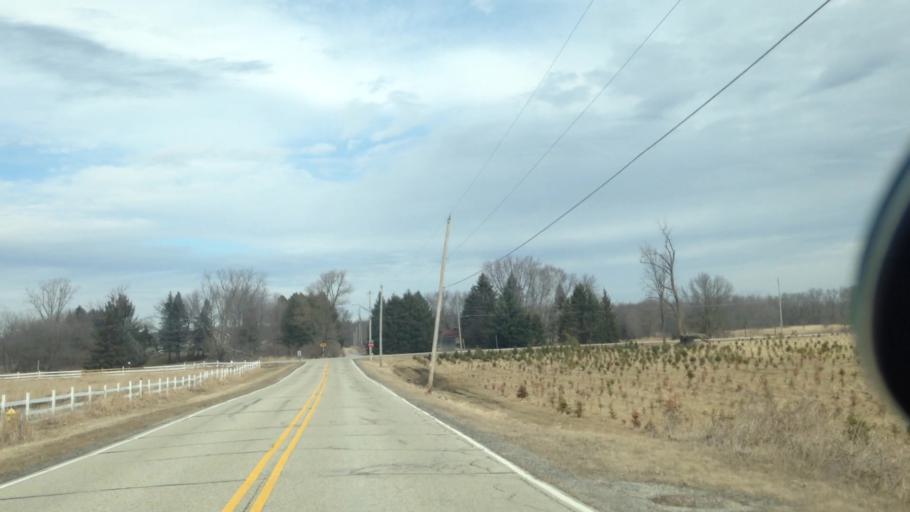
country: US
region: Wisconsin
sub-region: Waukesha County
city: Sussex
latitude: 43.1613
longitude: -88.2233
